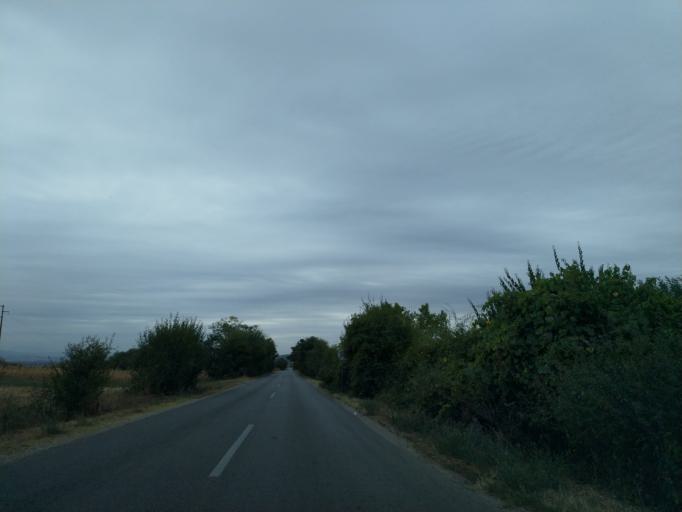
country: RS
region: Central Serbia
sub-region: Pomoravski Okrug
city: Jagodina
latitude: 44.0064
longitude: 21.2066
